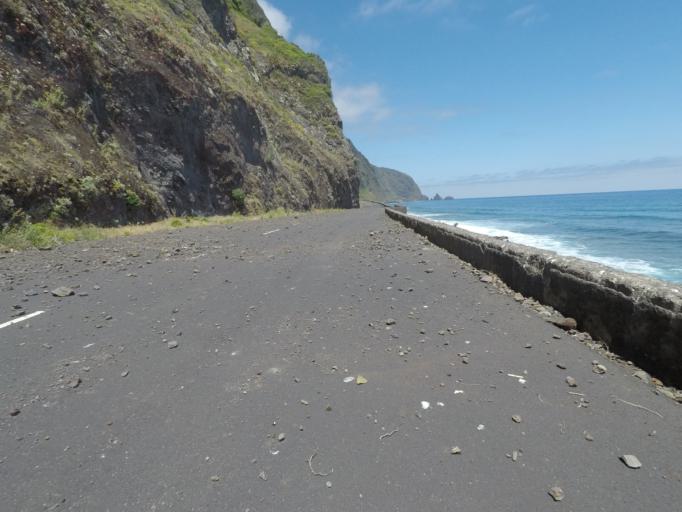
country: PT
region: Madeira
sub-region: Porto Moniz
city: Porto Moniz
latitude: 32.8275
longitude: -17.1253
